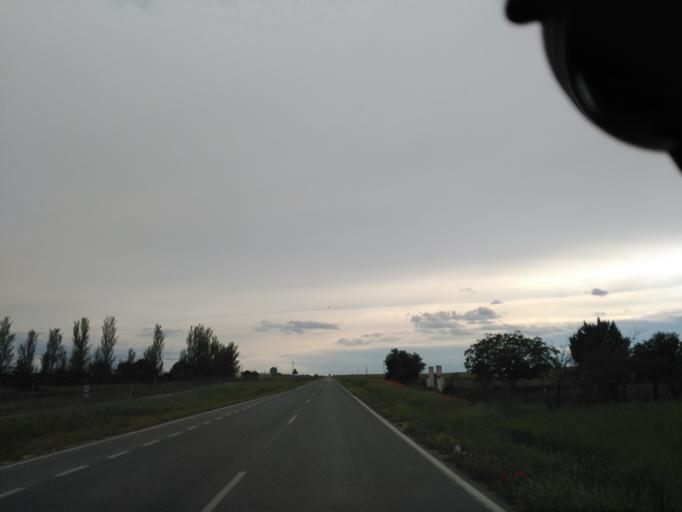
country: ES
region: Madrid
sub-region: Provincia de Madrid
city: Santorcaz
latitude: 40.4814
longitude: -3.2088
